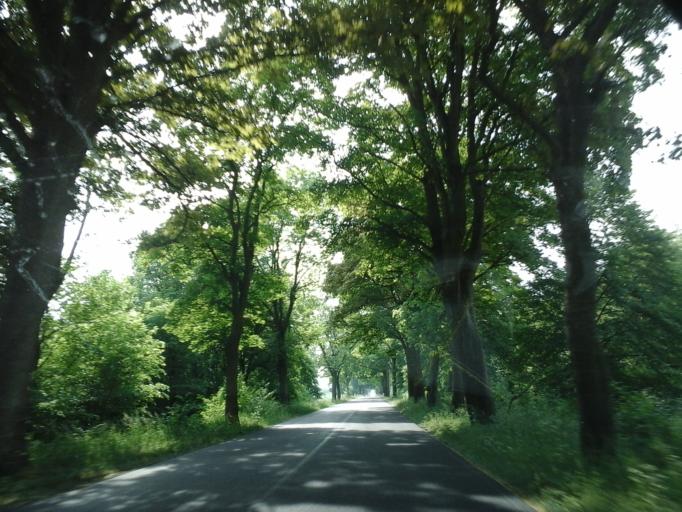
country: PL
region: West Pomeranian Voivodeship
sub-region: Powiat choszczenski
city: Recz
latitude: 53.1898
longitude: 15.6317
